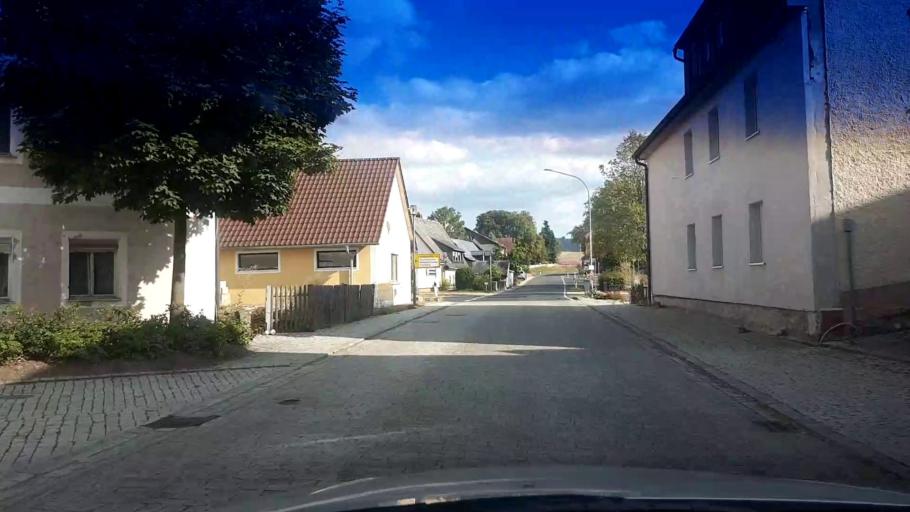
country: DE
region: Bavaria
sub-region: Upper Palatinate
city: Neualbenreuth
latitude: 49.9792
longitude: 12.4435
